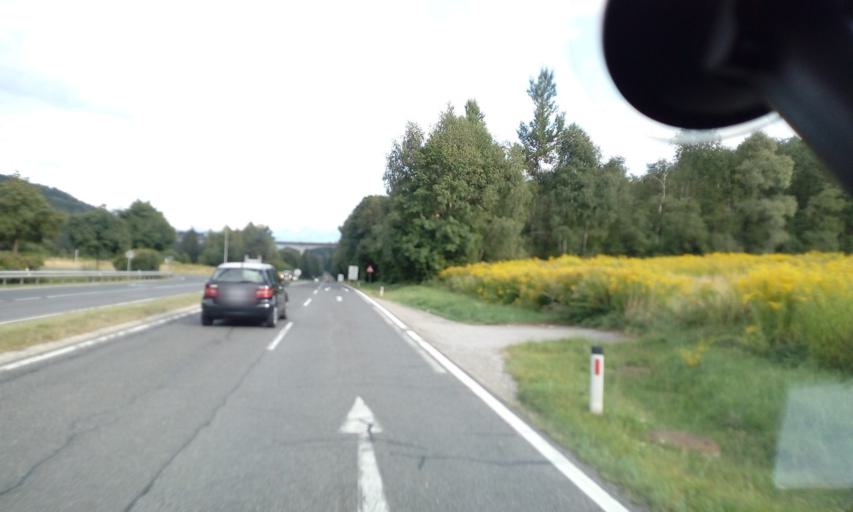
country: AT
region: Carinthia
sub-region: Villach Stadt
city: Villach
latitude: 46.6466
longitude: 13.7948
